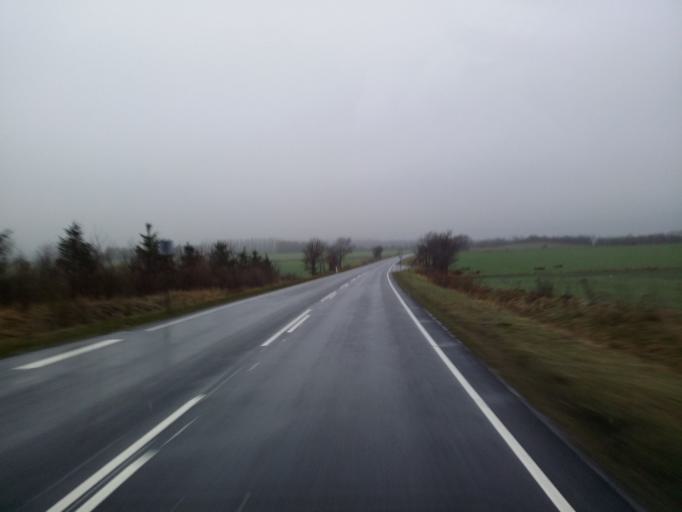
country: DK
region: Capital Region
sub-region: Frederikssund Kommune
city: Jaegerspris
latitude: 55.8239
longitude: 12.0077
